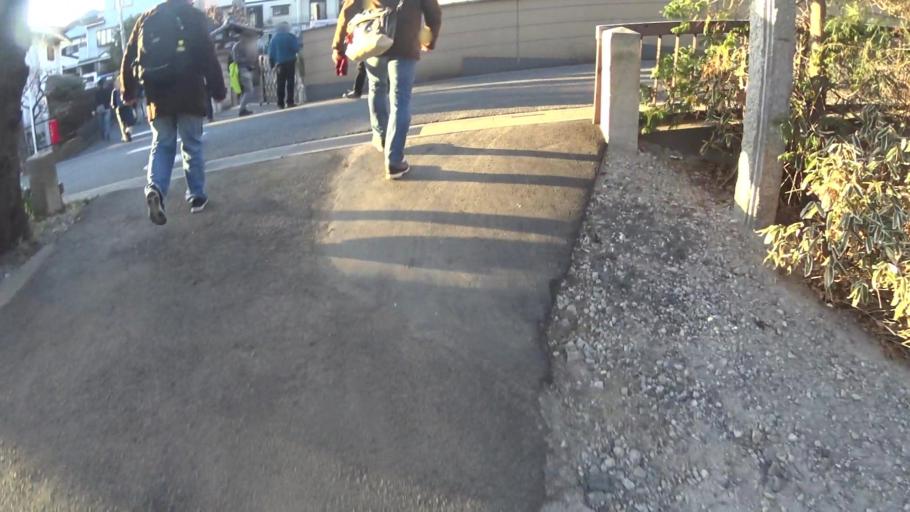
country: JP
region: Saitama
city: Shimotoda
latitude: 35.8520
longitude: 139.6840
